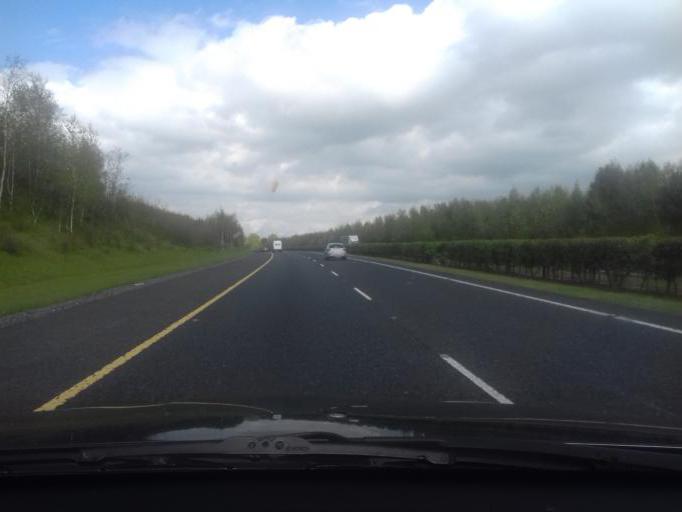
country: IE
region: Leinster
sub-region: Kildare
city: Monasterevin
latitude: 53.1150
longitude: -7.0540
